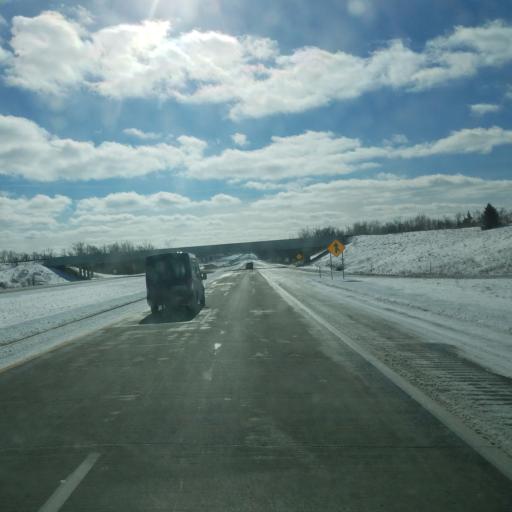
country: US
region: Michigan
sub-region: Clinton County
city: DeWitt
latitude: 42.8581
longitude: -84.5190
